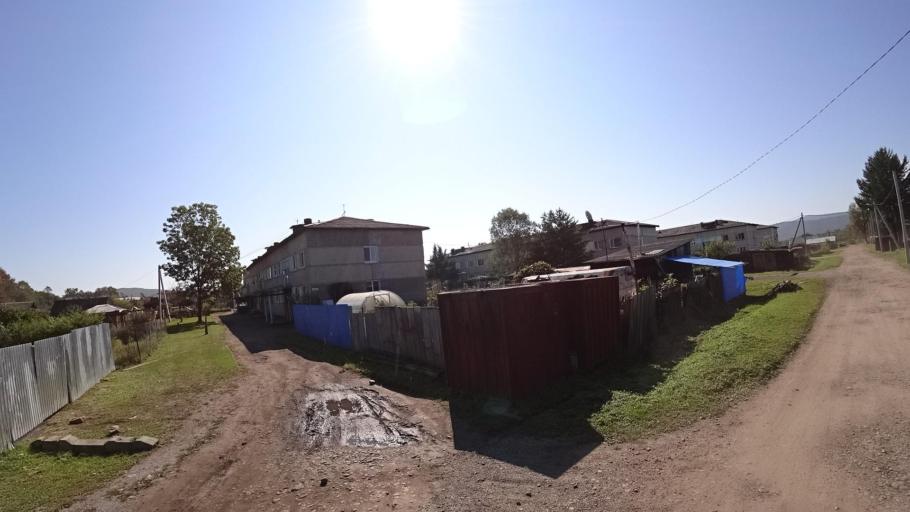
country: RU
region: Jewish Autonomous Oblast
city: Bira
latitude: 48.9988
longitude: 132.4521
